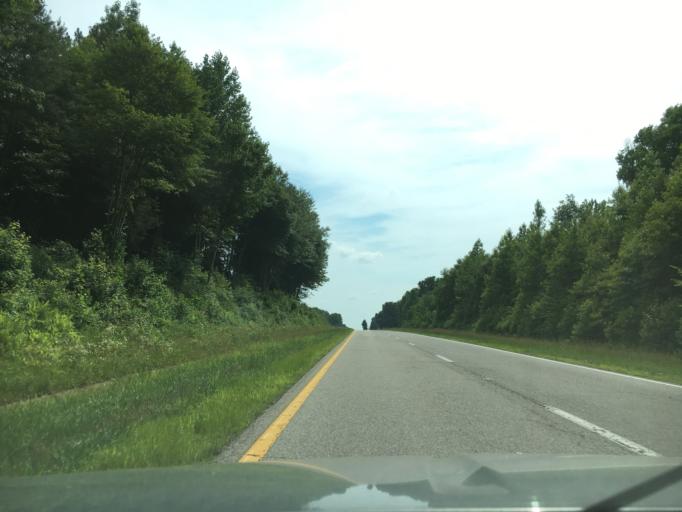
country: US
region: Virginia
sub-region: Nottoway County
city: Crewe
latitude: 37.1566
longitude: -78.2741
